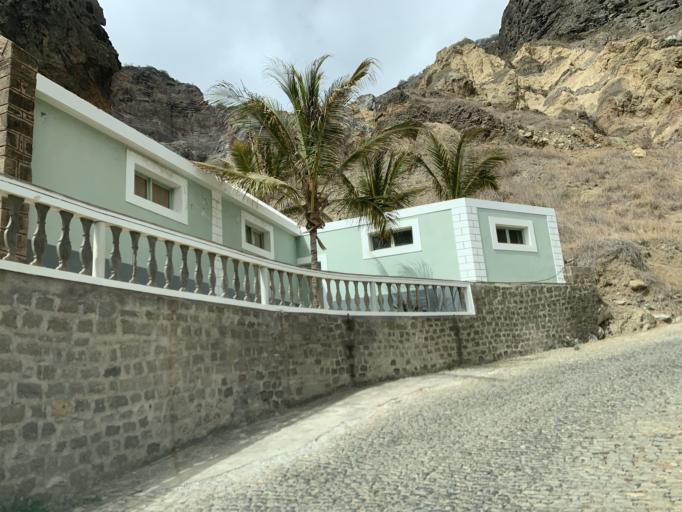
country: CV
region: Brava
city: Vila Nova Sintra
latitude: 14.8739
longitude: -24.7314
